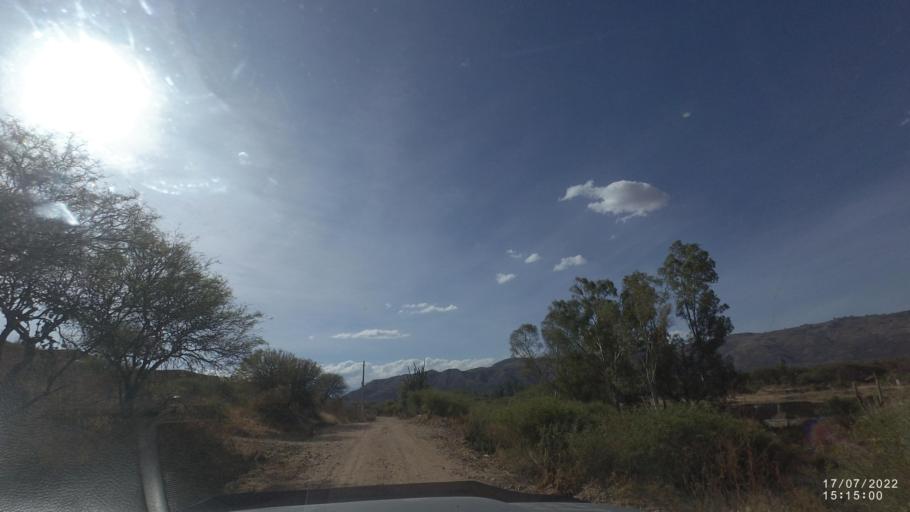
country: BO
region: Cochabamba
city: Capinota
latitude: -17.5594
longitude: -66.2617
